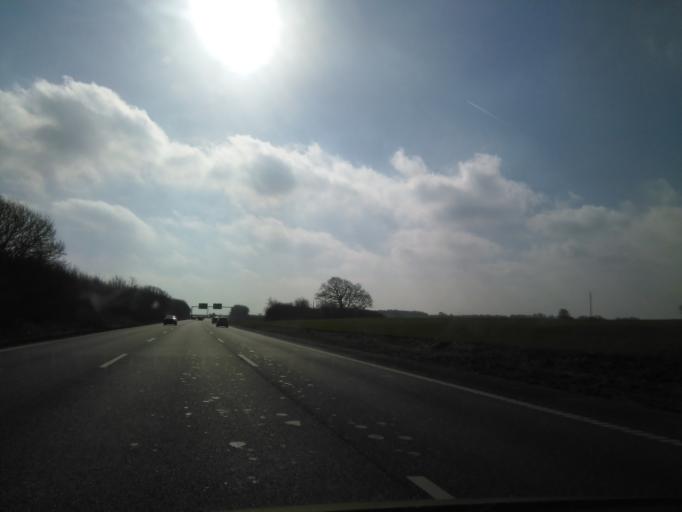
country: DK
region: South Denmark
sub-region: Fredericia Kommune
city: Taulov
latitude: 55.6075
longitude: 9.5840
